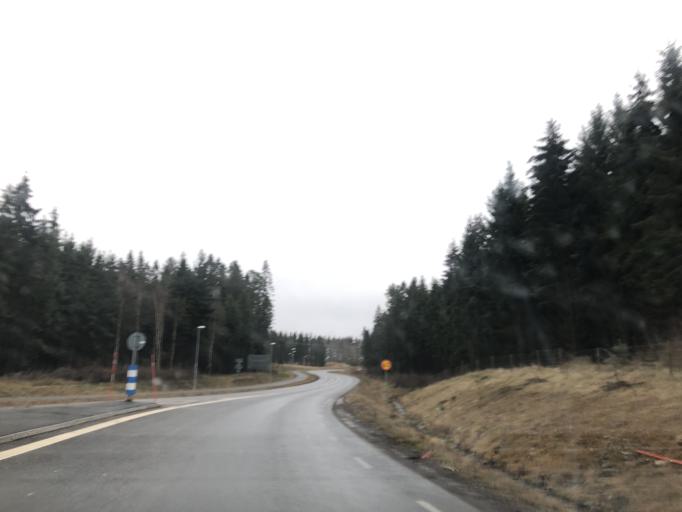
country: SE
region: Vaestra Goetaland
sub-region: Ulricehamns Kommun
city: Ulricehamn
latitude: 57.8175
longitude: 13.2867
